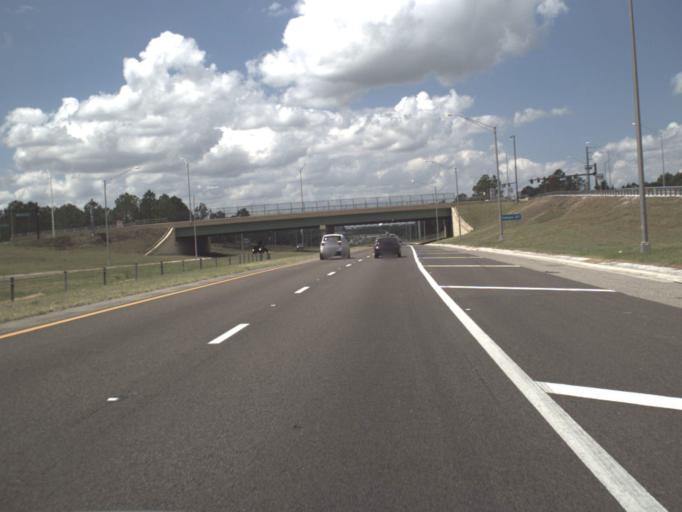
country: US
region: Florida
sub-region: Orange County
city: Paradise Heights
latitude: 28.6025
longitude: -81.5414
